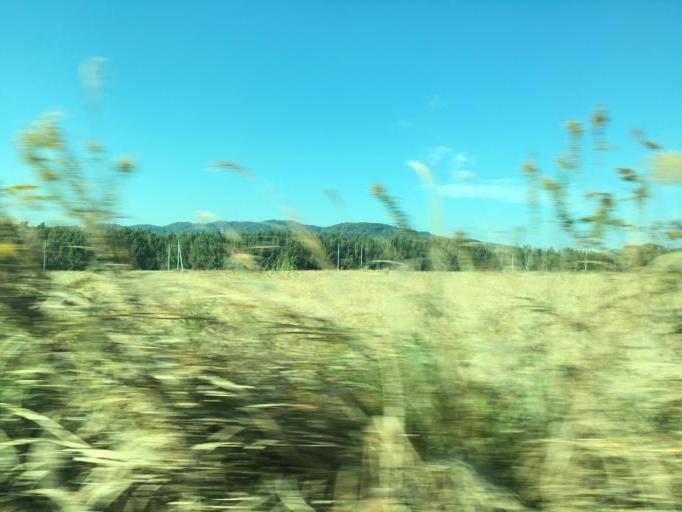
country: JP
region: Ibaraki
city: Iwase
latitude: 36.3532
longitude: 140.0876
